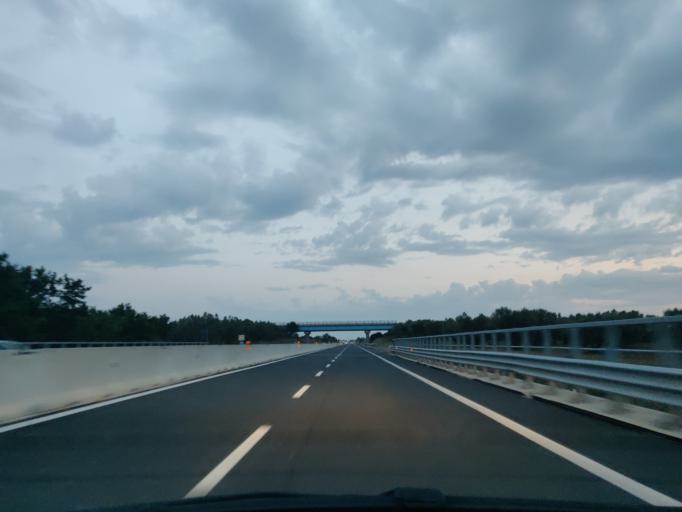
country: IT
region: Latium
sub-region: Provincia di Viterbo
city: Blera
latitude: 42.3422
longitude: 11.9826
